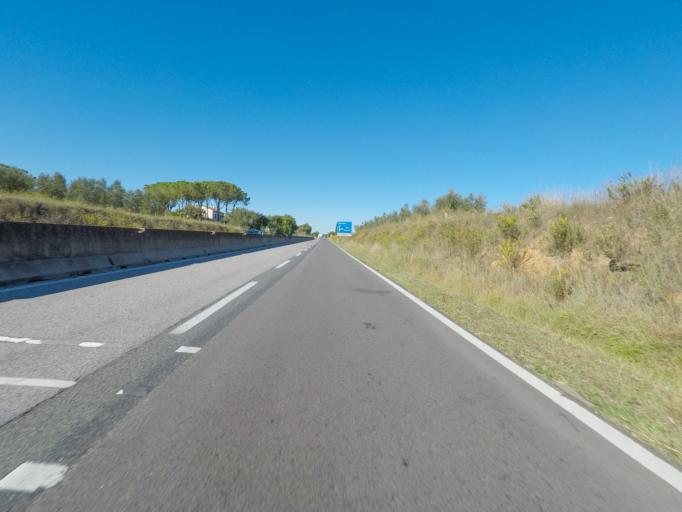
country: IT
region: Tuscany
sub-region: Provincia di Grosseto
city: Grosseto
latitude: 42.6866
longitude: 11.1391
